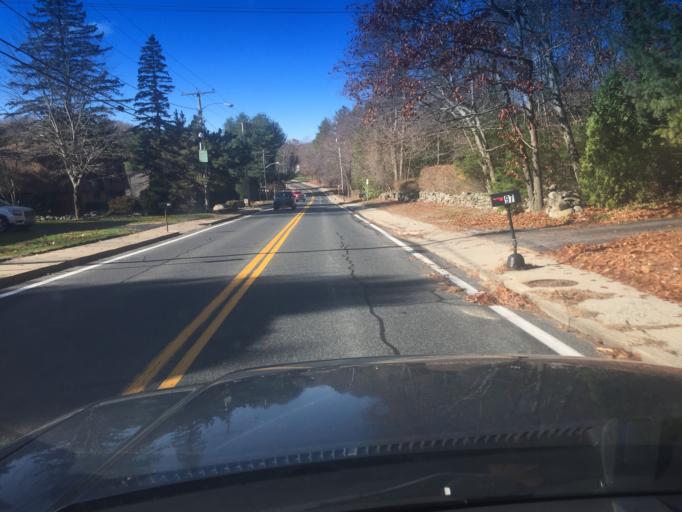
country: US
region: Rhode Island
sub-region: Providence County
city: Greenville
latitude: 41.8647
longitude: -71.5677
